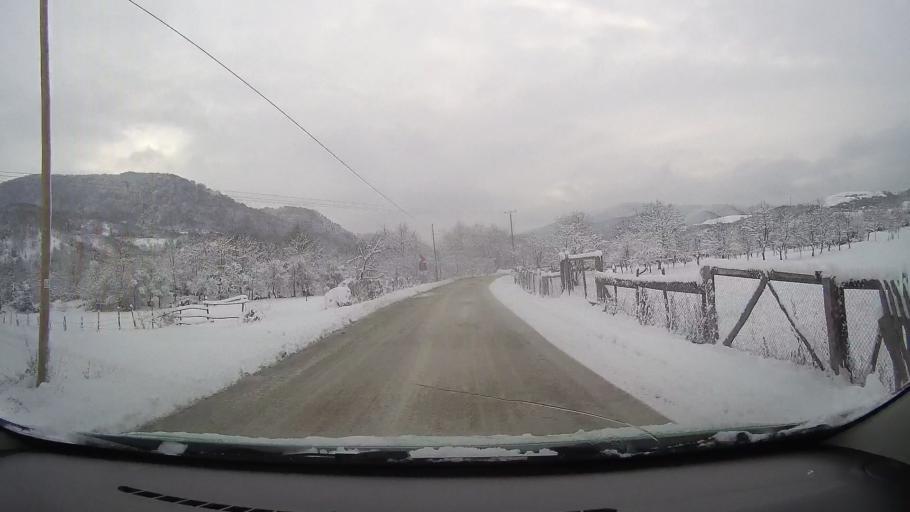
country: RO
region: Alba
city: Pianu de Sus
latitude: 45.9069
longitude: 23.4804
